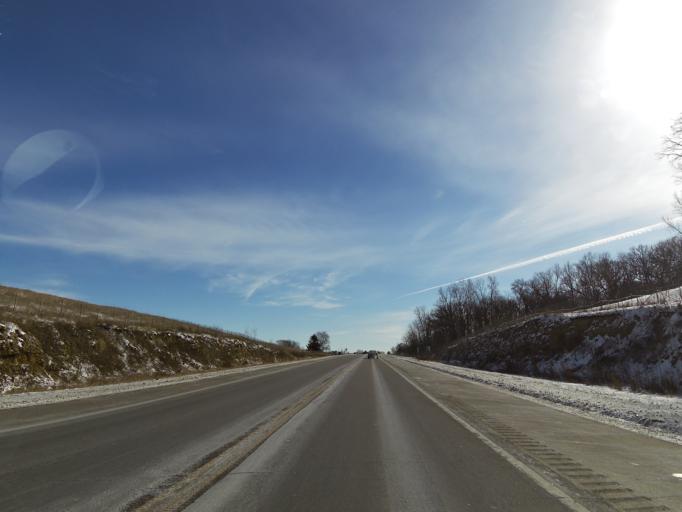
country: US
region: Minnesota
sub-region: Dakota County
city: Hastings
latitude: 44.7585
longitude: -92.8404
